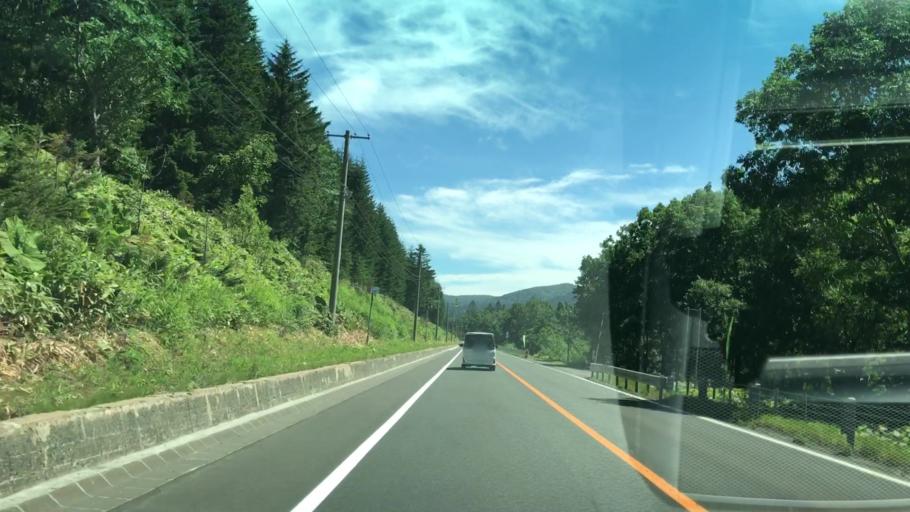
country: JP
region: Hokkaido
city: Shimo-furano
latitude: 42.9750
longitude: 142.6882
